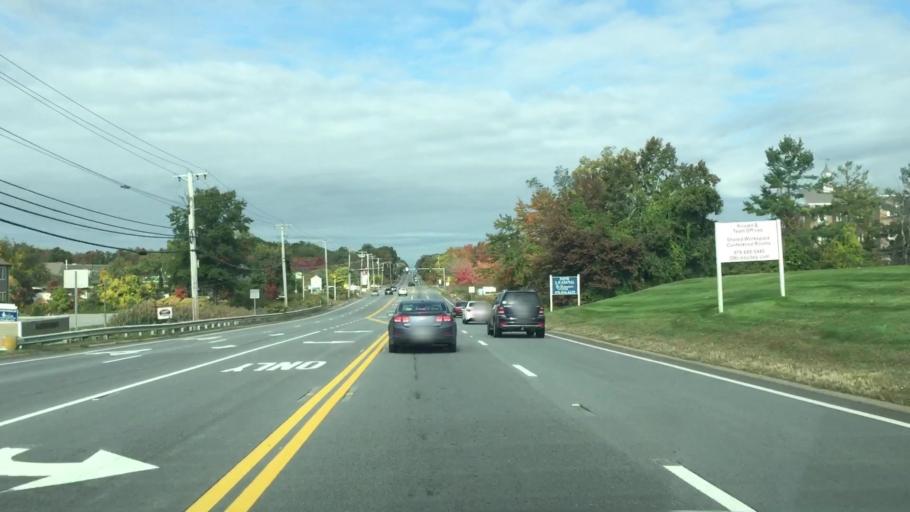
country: US
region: Massachusetts
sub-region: Essex County
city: Andover
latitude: 42.6593
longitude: -71.1066
